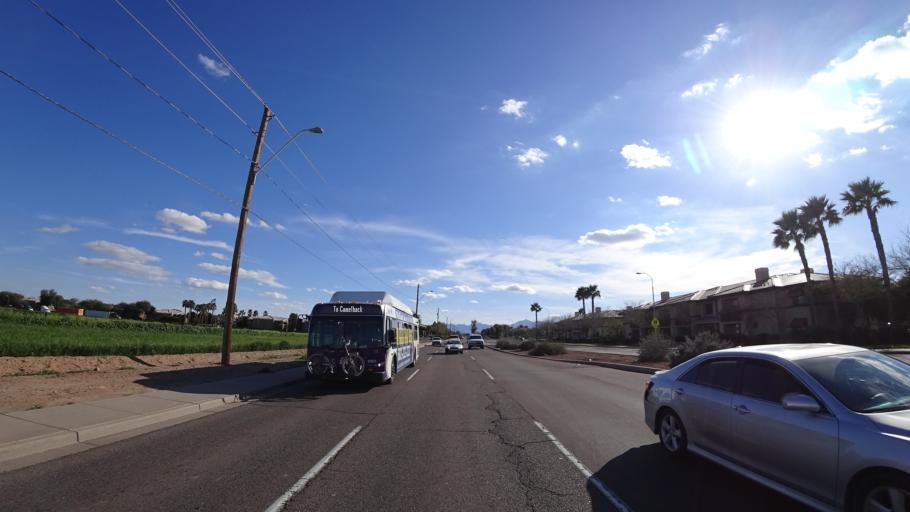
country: US
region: Arizona
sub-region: Maricopa County
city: Tolleson
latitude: 33.4775
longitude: -112.2377
